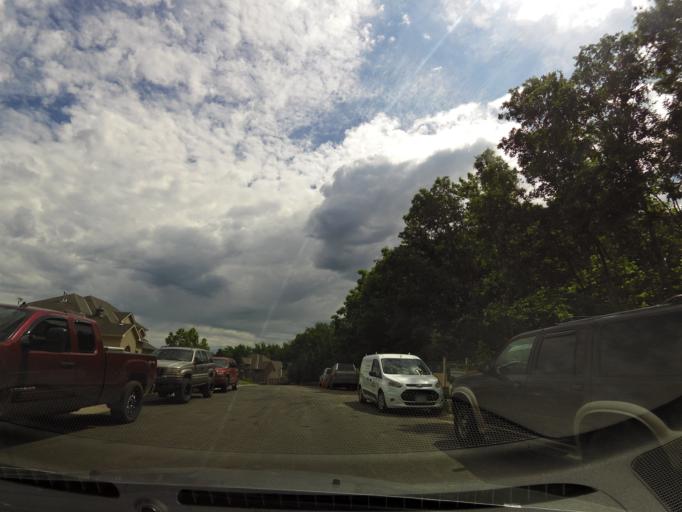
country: US
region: Minnesota
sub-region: Scott County
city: Prior Lake
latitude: 44.7551
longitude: -93.4526
